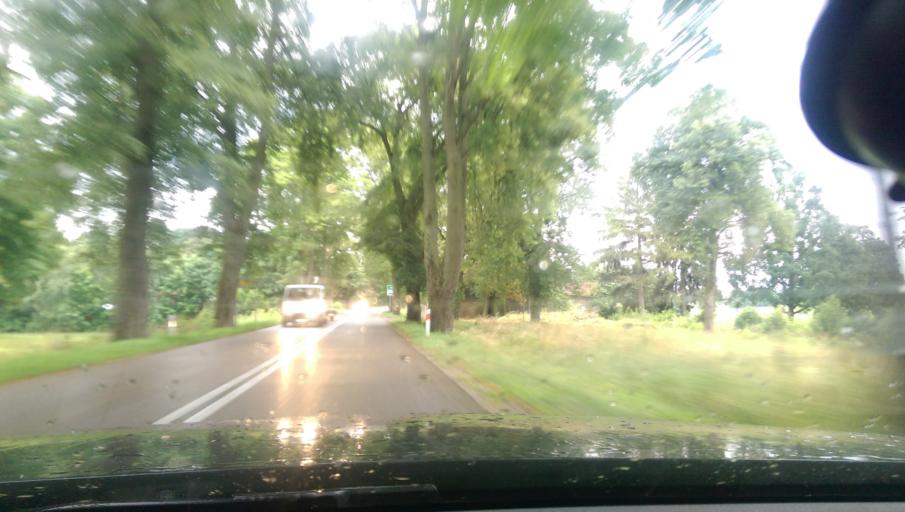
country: PL
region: Warmian-Masurian Voivodeship
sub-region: Powiat piski
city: Ruciane-Nida
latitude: 53.6900
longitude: 21.4841
